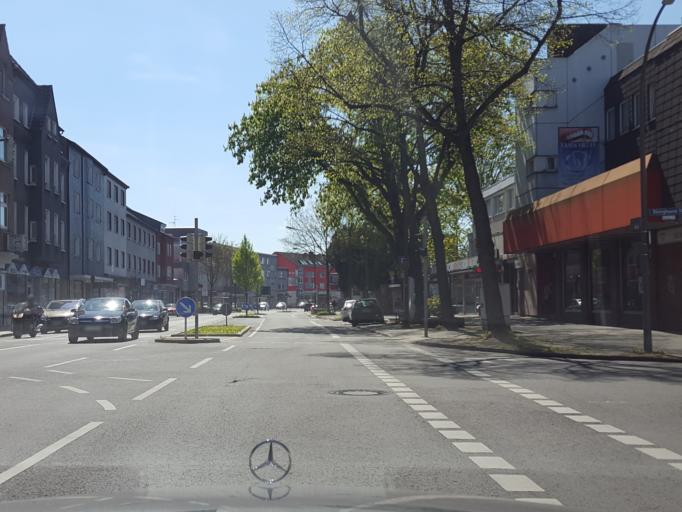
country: DE
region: North Rhine-Westphalia
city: Castrop-Rauxel
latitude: 51.5213
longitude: 7.3252
